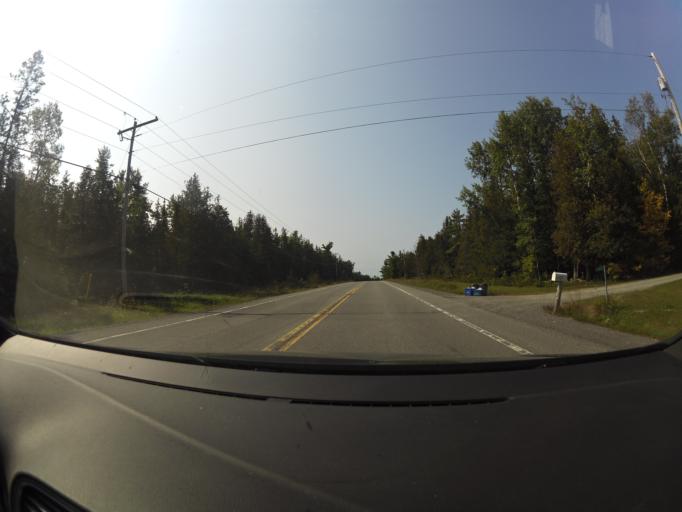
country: CA
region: Ontario
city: Arnprior
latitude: 45.4835
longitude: -76.1584
